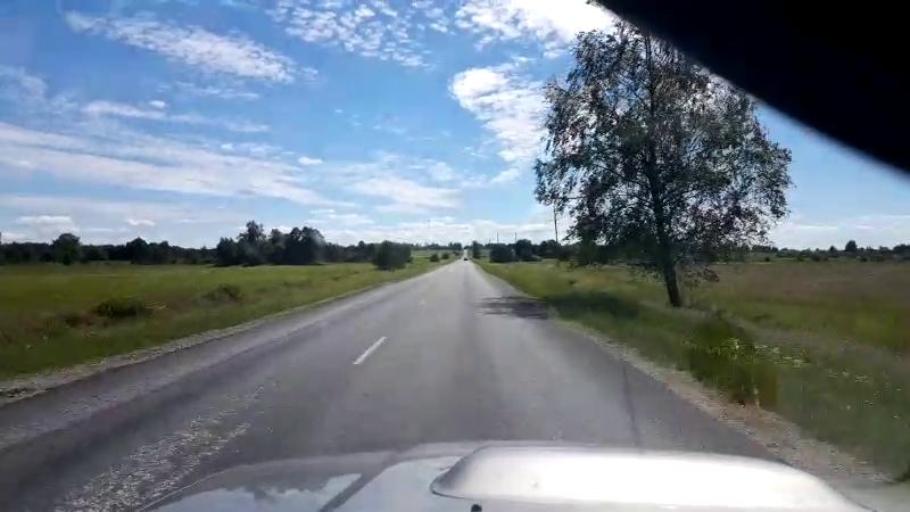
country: EE
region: Laeaene-Virumaa
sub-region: Rakke vald
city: Rakke
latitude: 58.8645
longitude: 26.2940
